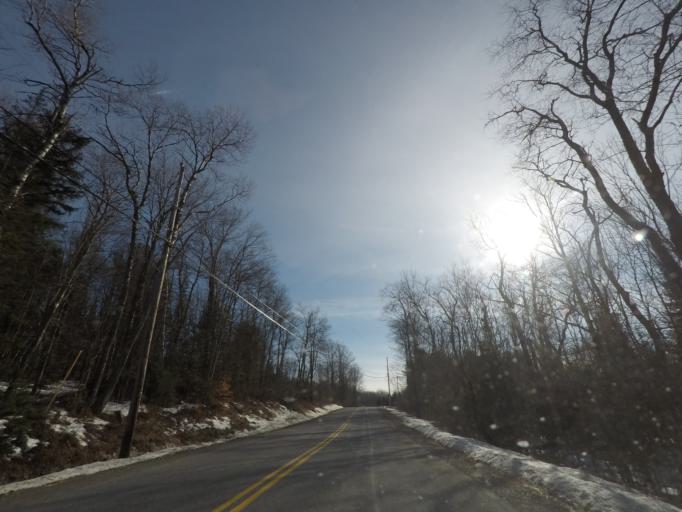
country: US
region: New York
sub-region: Rensselaer County
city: Poestenkill
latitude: 42.6953
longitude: -73.4225
